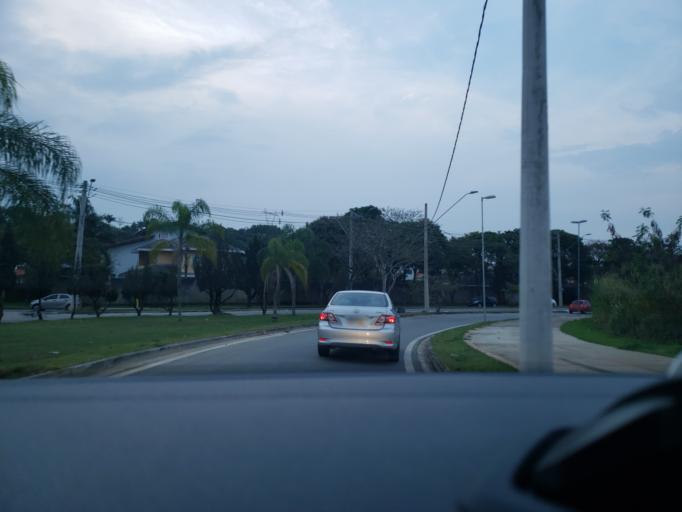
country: BR
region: Sao Paulo
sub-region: Sao Jose Dos Campos
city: Sao Jose dos Campos
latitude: -23.1953
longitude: -45.9318
